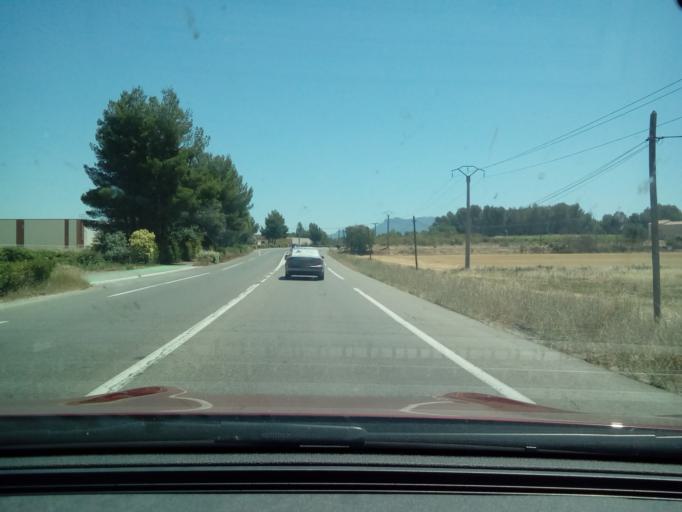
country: FR
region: Provence-Alpes-Cote d'Azur
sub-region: Departement des Bouches-du-Rhone
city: Rousset
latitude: 43.4629
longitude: 5.6161
